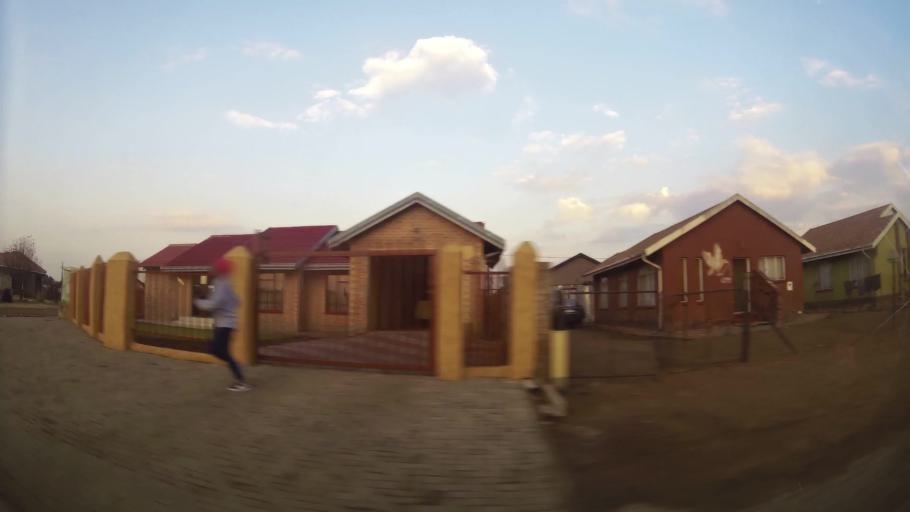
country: ZA
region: Gauteng
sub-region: City of Johannesburg Metropolitan Municipality
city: Orange Farm
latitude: -26.5445
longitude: 27.8852
